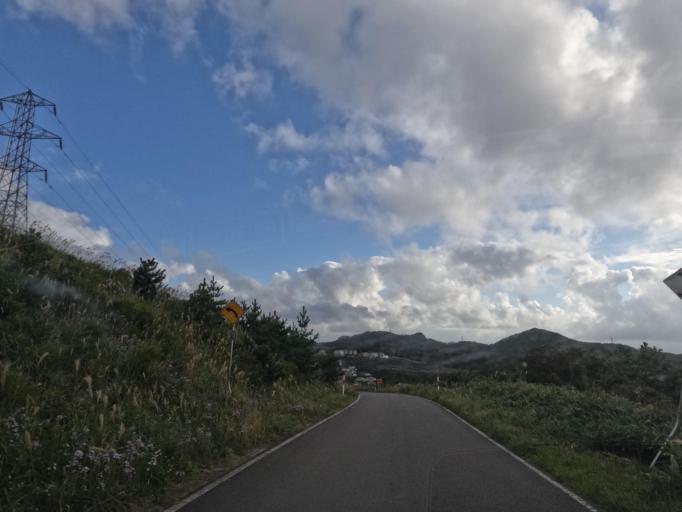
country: JP
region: Hokkaido
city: Muroran
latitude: 42.3149
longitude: 141.0056
